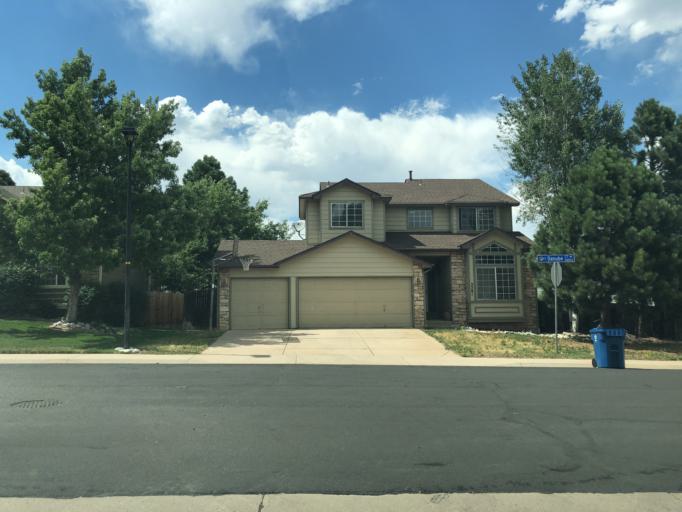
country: US
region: Colorado
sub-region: Arapahoe County
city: Dove Valley
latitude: 39.6187
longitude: -104.7640
